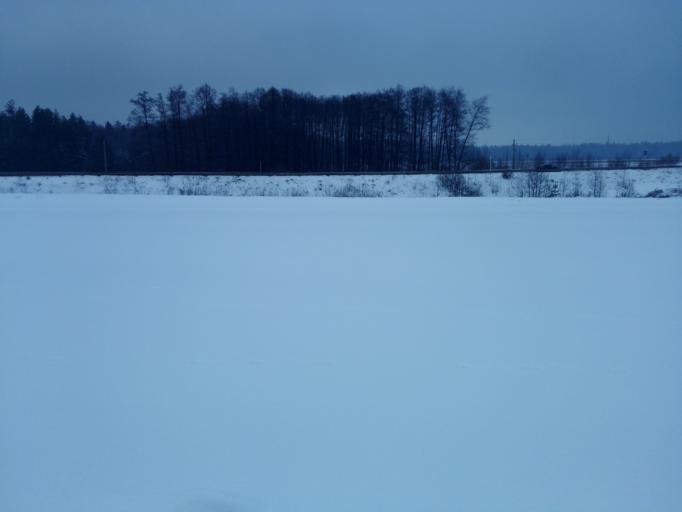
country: RU
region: Vladimir
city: Kommunar
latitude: 56.0640
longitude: 40.5032
